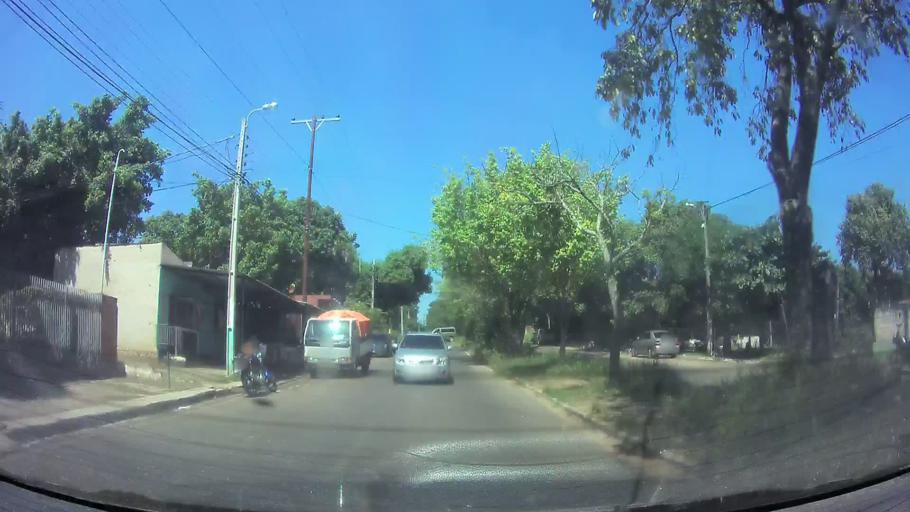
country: PY
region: Central
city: Fernando de la Mora
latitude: -25.2862
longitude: -57.5198
